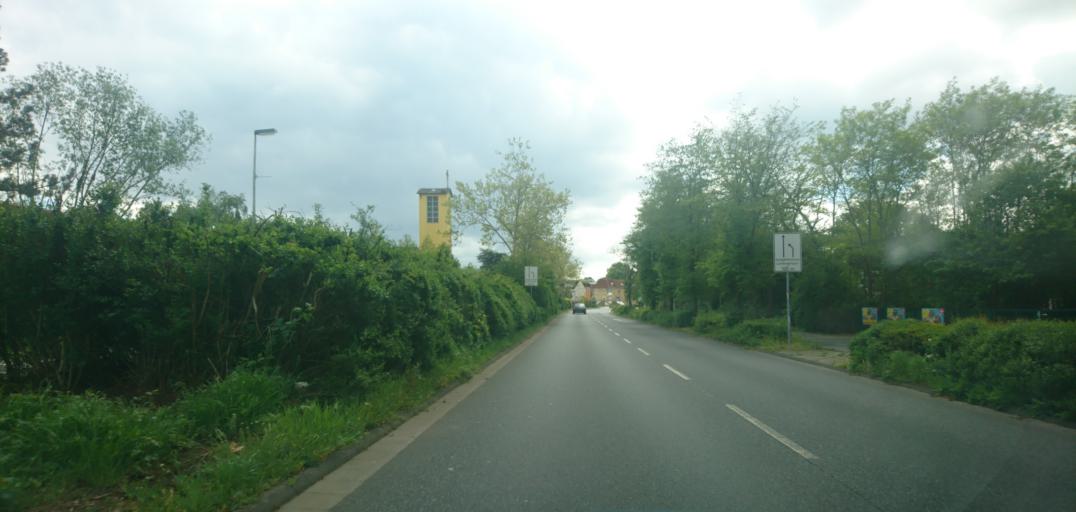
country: DE
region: Hesse
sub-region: Regierungsbezirk Darmstadt
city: Dietzenbach
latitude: 50.0127
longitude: 8.7779
